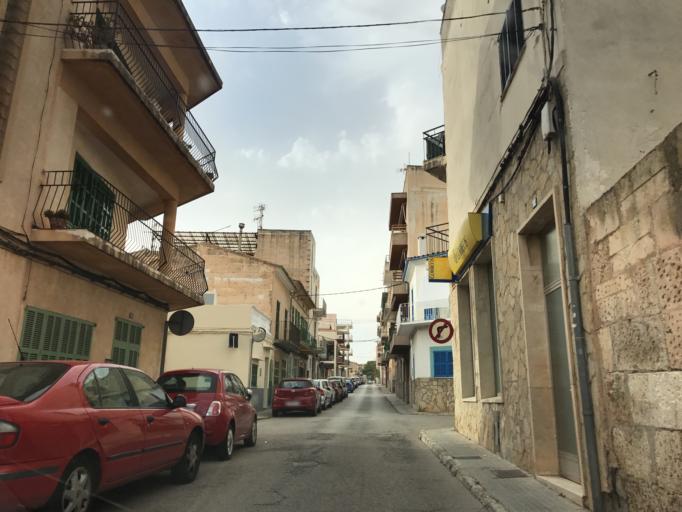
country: ES
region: Balearic Islands
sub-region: Illes Balears
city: Son Servera
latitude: 39.5418
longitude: 3.3330
